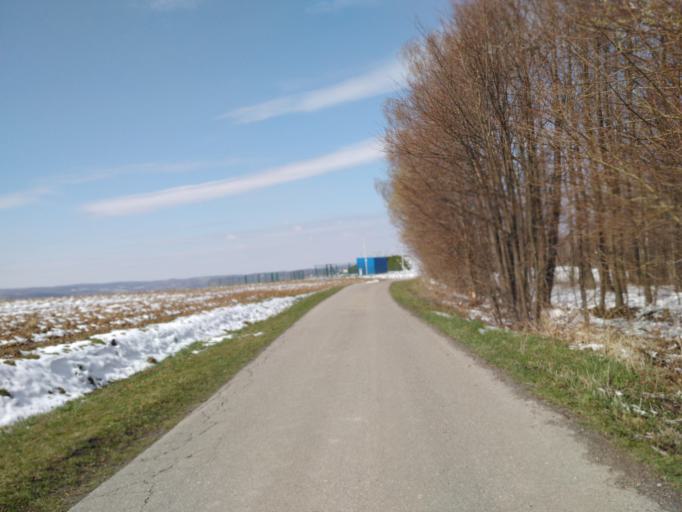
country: PL
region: Subcarpathian Voivodeship
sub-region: Powiat ropczycko-sedziszowski
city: Wielopole Skrzynskie
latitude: 49.9922
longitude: 21.5903
